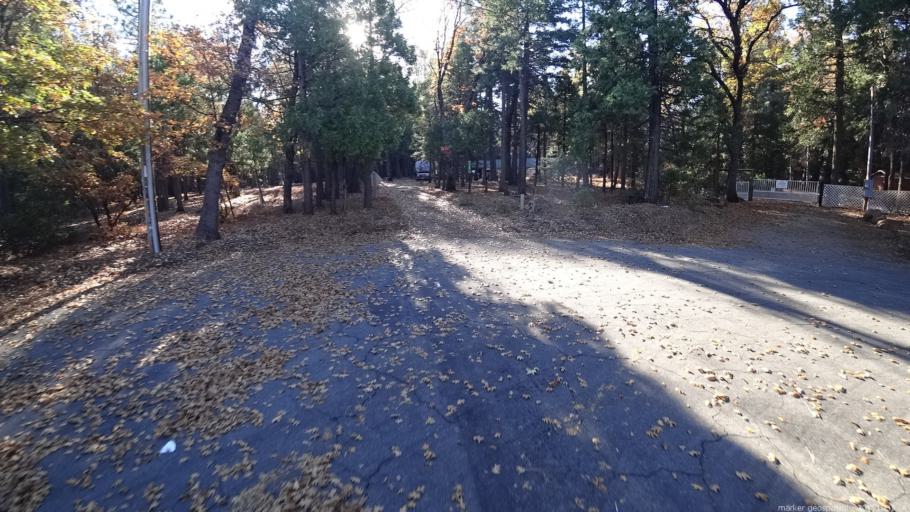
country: US
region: California
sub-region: Shasta County
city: Shingletown
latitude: 40.5216
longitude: -121.8361
